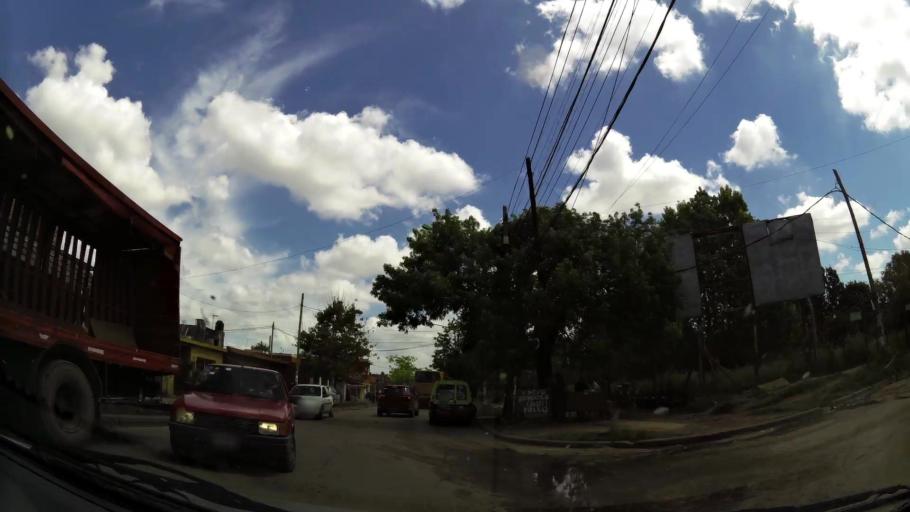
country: AR
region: Buenos Aires
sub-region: Partido de Quilmes
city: Quilmes
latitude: -34.8060
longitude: -58.2495
